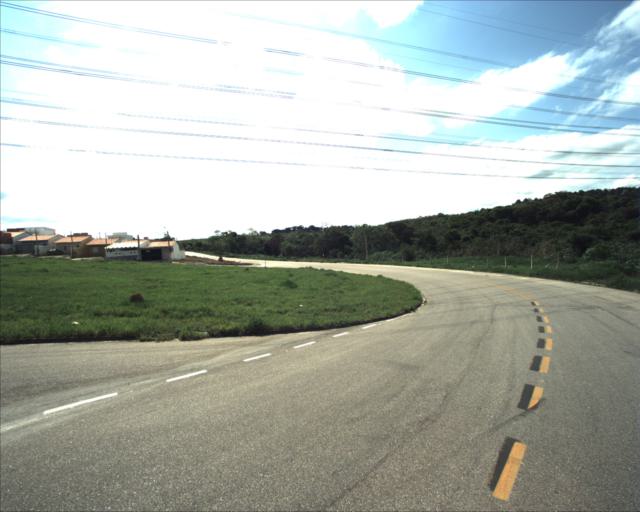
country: BR
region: Sao Paulo
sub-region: Sorocaba
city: Sorocaba
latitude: -23.3910
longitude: -47.3764
